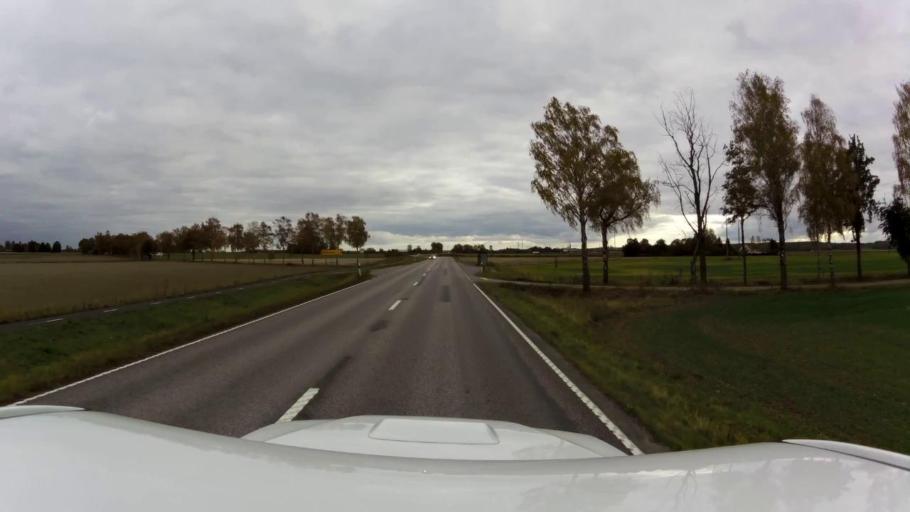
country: SE
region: OEstergoetland
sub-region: Linkopings Kommun
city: Berg
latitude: 58.4465
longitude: 15.5645
